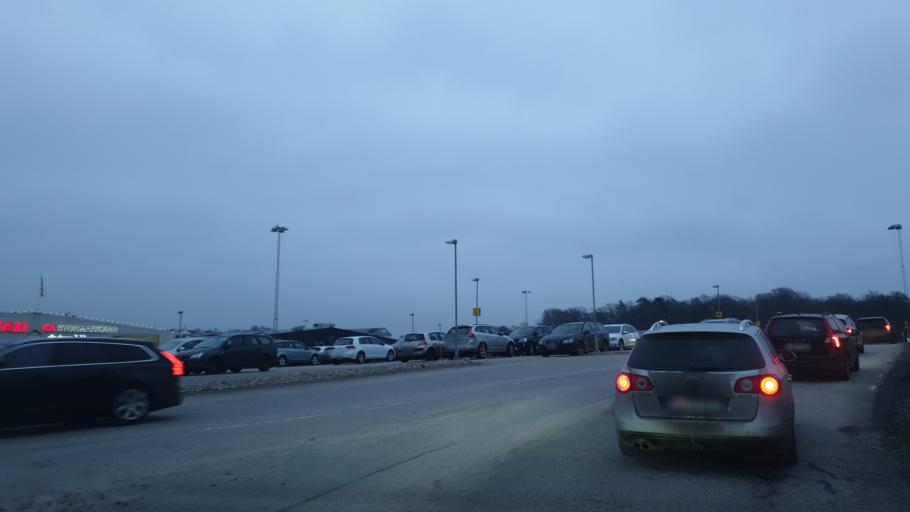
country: SE
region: Blekinge
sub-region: Karlskrona Kommun
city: Karlskrona
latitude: 56.1957
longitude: 15.6389
